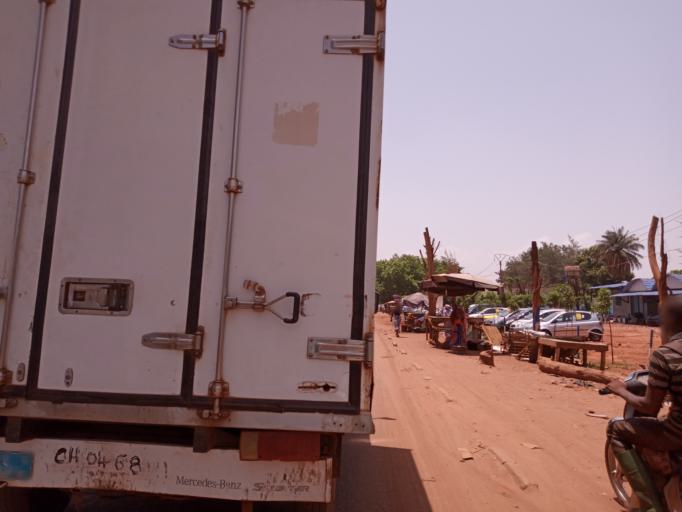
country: ML
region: Bamako
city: Bamako
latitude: 12.6504
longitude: -7.9609
